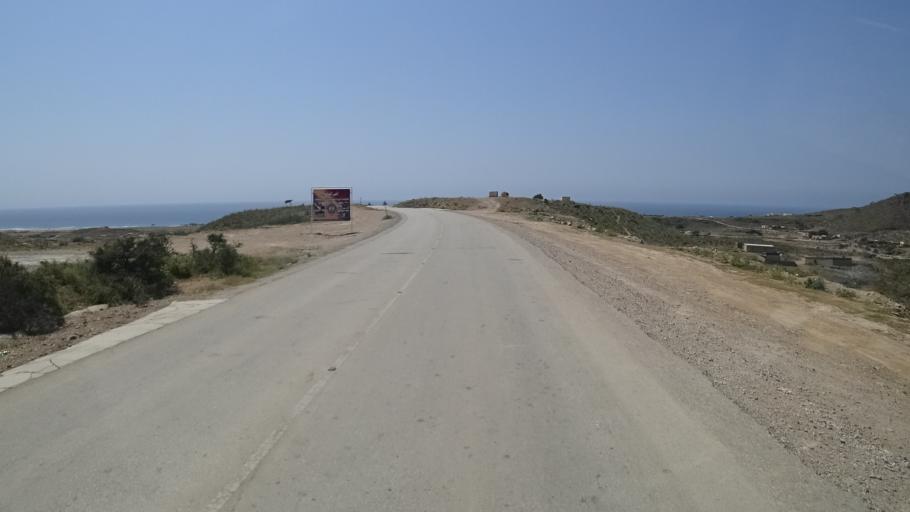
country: OM
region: Zufar
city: Salalah
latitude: 17.0424
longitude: 54.6127
